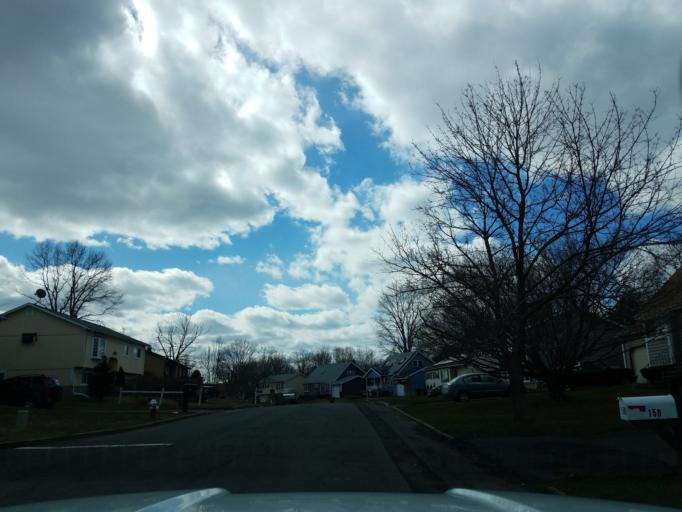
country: US
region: Connecticut
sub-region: New Haven County
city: Prospect
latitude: 41.4817
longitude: -73.0099
